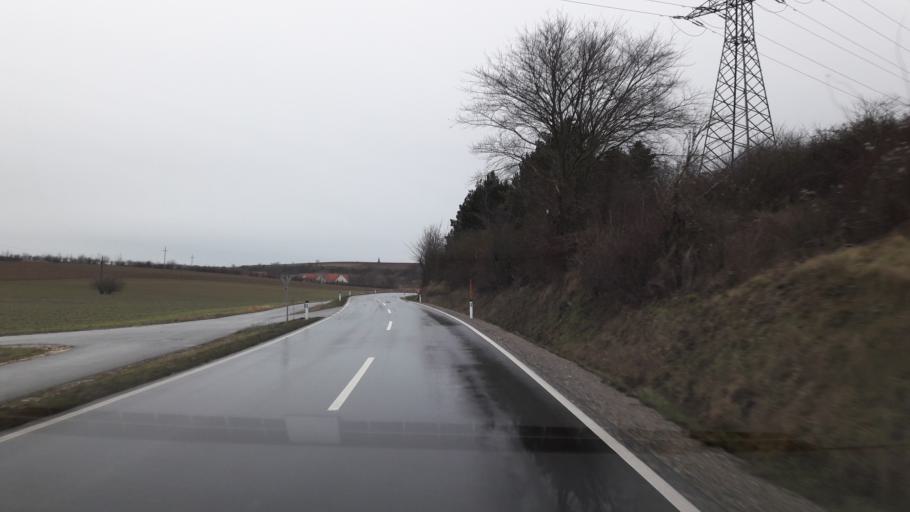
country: AT
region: Lower Austria
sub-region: Politischer Bezirk Mistelbach
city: Hochleithen
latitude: 48.4361
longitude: 16.5429
